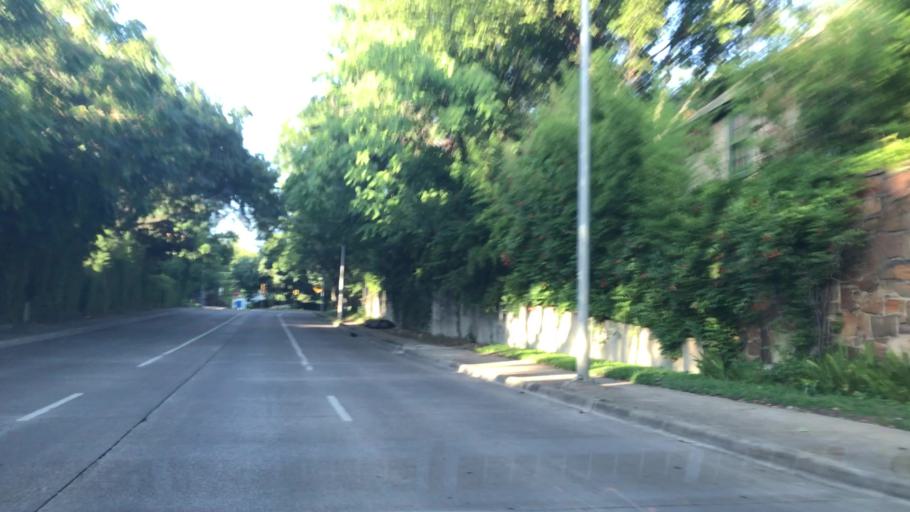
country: US
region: Texas
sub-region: Dallas County
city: Highland Park
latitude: 32.8177
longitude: -96.7983
